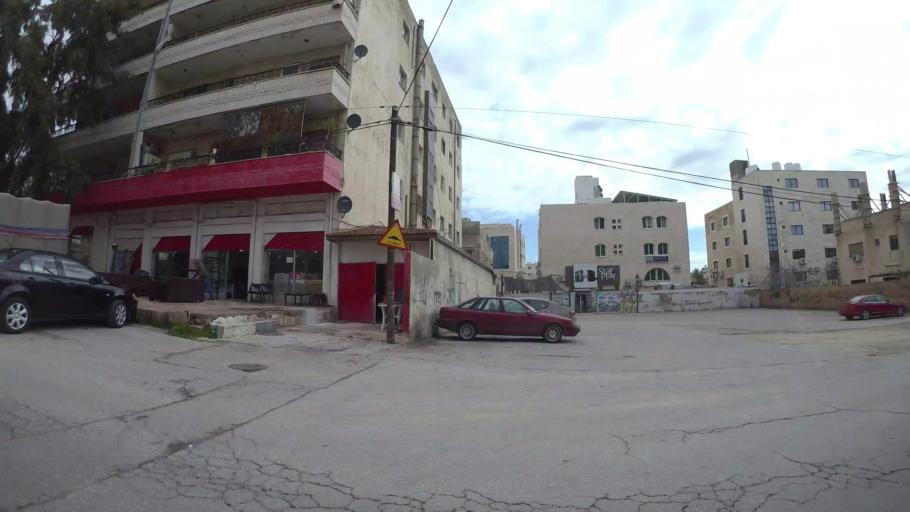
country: JO
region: Amman
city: Wadi as Sir
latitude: 31.9525
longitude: 35.8396
